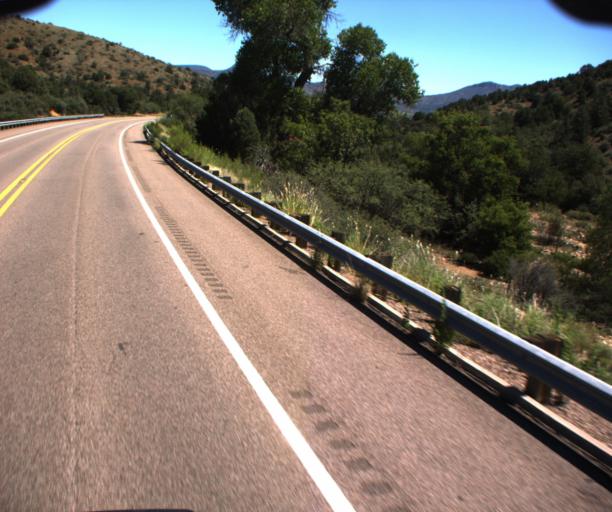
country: US
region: Arizona
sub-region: Gila County
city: Globe
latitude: 33.5619
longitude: -110.6766
